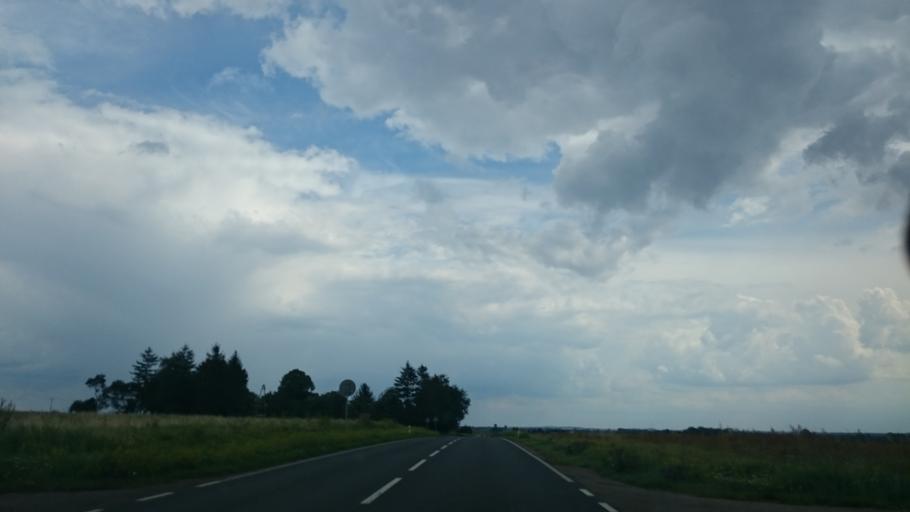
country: PL
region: Kujawsko-Pomorskie
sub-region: Powiat tucholski
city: Kesowo
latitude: 53.6628
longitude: 17.6729
